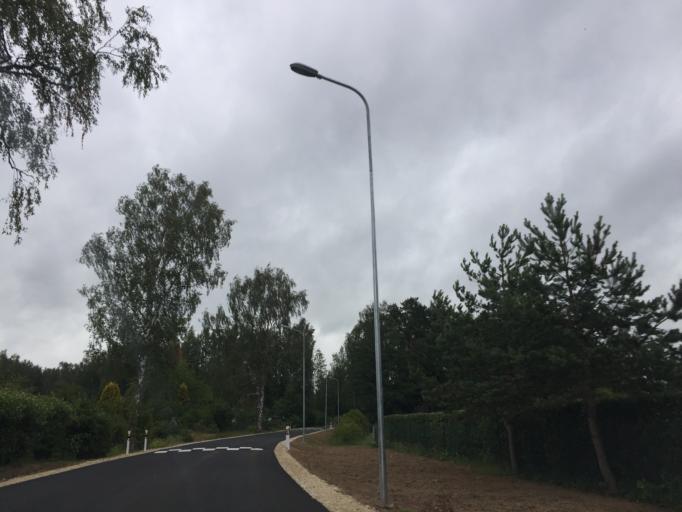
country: LV
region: Carnikava
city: Carnikava
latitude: 57.1174
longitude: 24.2303
